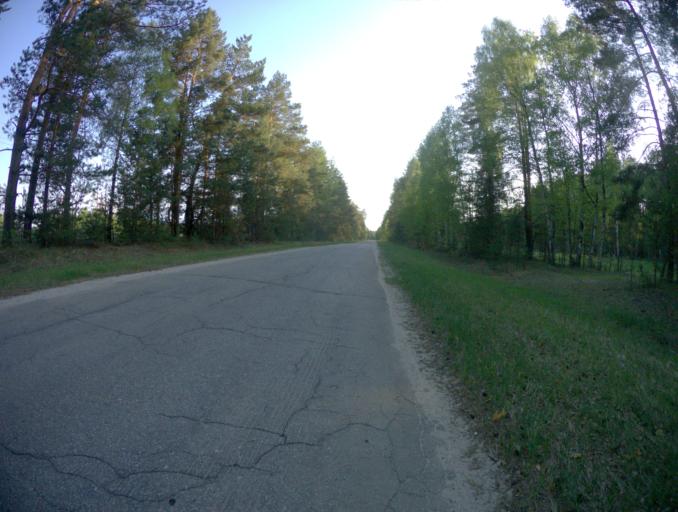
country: RU
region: Vladimir
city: Vyazniki
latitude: 56.3413
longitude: 42.1390
